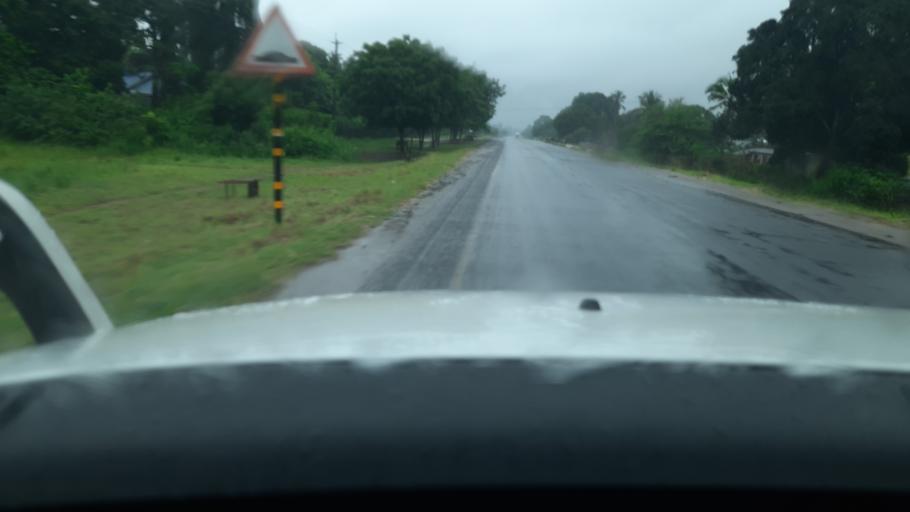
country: TZ
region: Pwani
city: Bagamoyo
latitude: -6.5479
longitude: 38.9961
